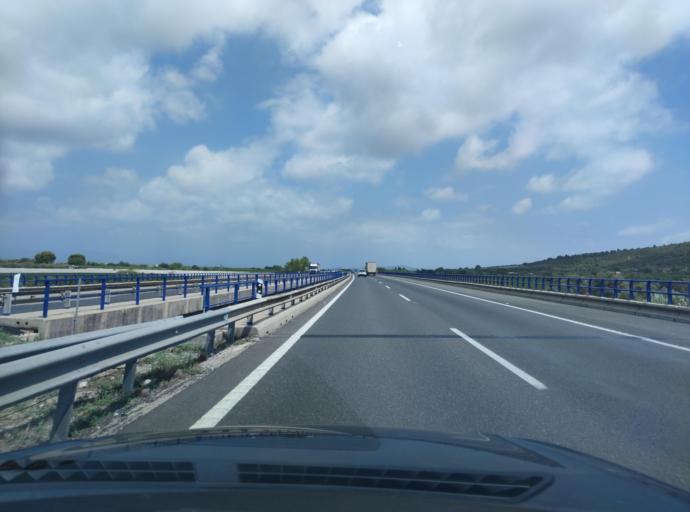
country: ES
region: Valencia
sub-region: Provincia de Castello
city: Vinaros
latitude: 40.5008
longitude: 0.4160
